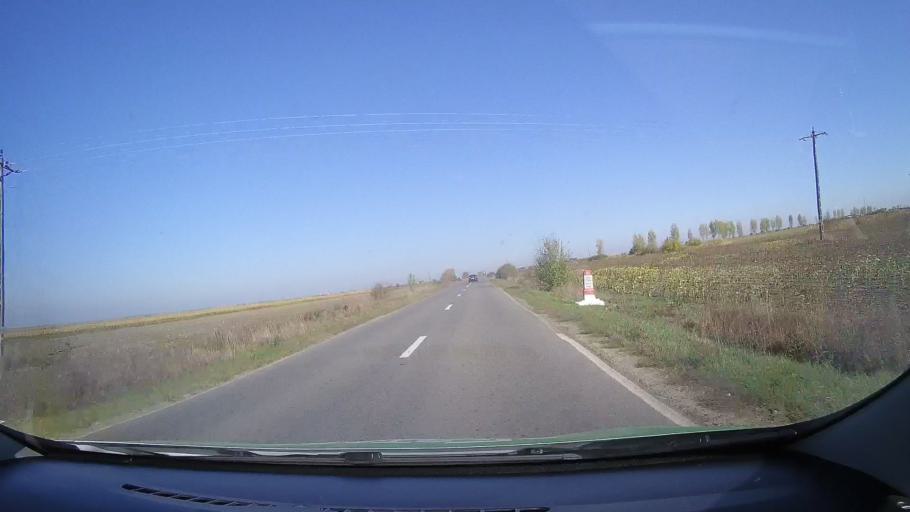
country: RO
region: Satu Mare
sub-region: Comuna Cauas
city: Cauas
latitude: 47.5944
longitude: 22.5466
